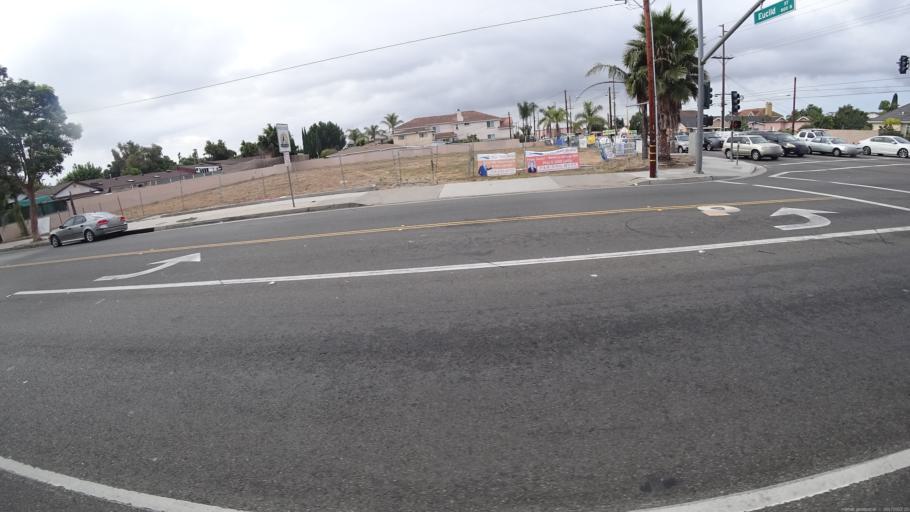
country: US
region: California
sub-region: Orange County
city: Garden Grove
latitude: 33.7524
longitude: -117.9373
